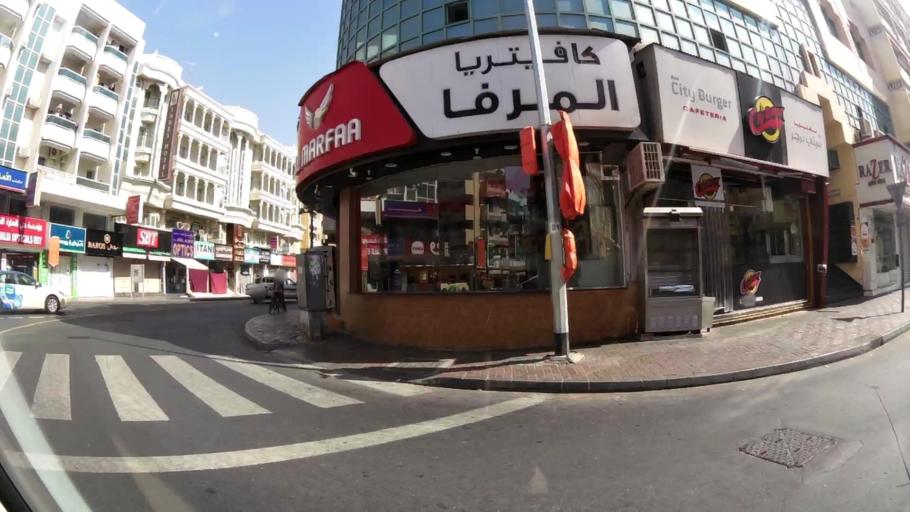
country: AE
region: Ash Shariqah
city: Sharjah
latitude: 25.2716
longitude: 55.3027
